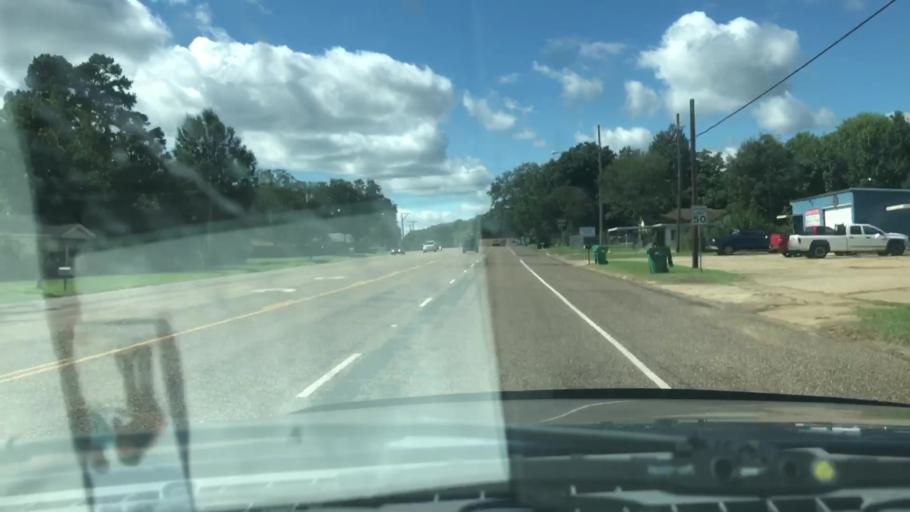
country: US
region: Texas
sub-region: Bowie County
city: Texarkana
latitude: 33.4027
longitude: -94.0743
